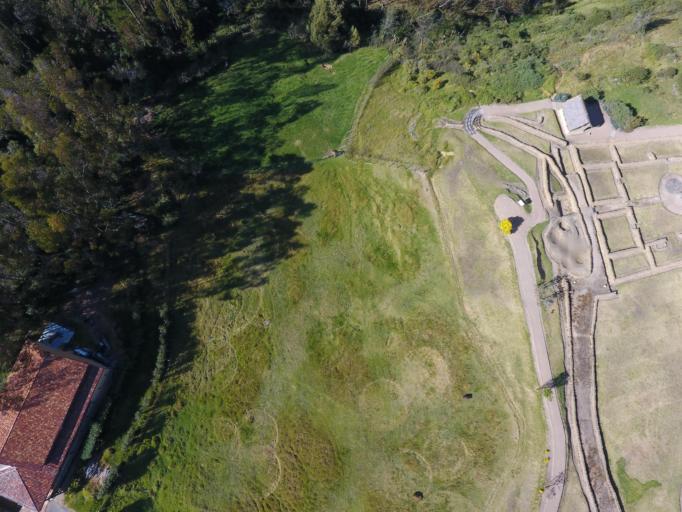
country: EC
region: Canar
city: Canar
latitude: -2.5412
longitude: -78.8730
